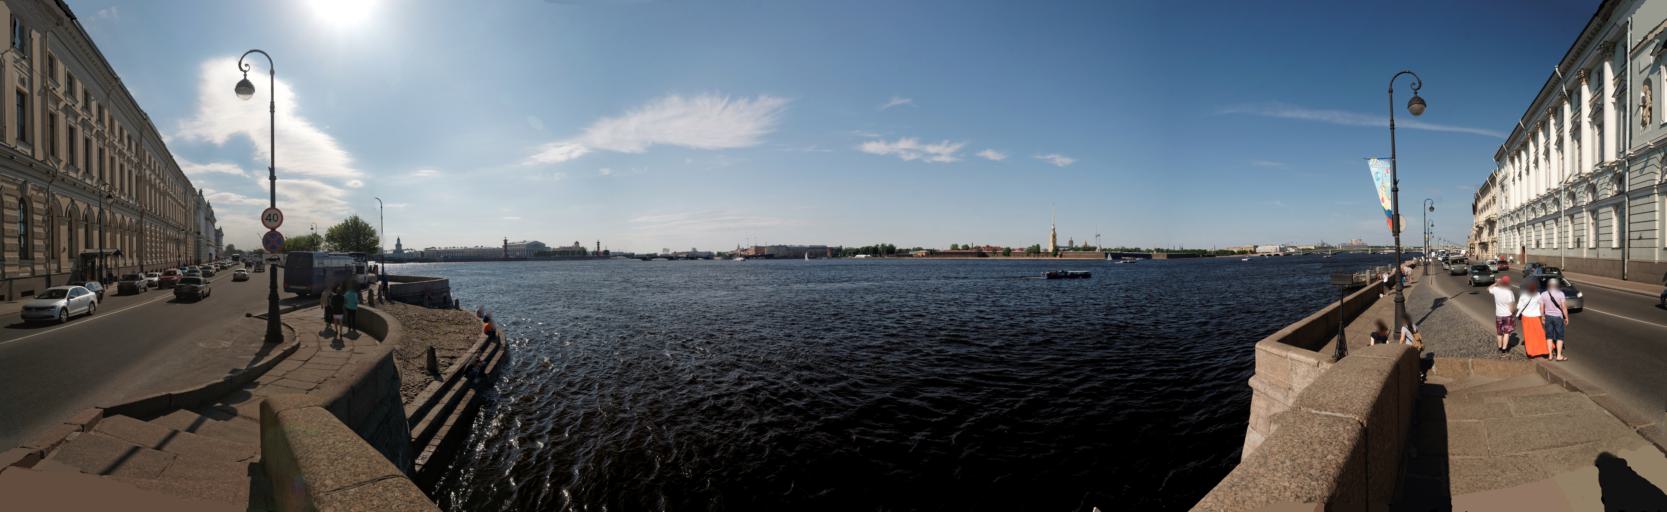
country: RU
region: St.-Petersburg
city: Saint Petersburg
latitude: 59.9426
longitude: 30.3161
